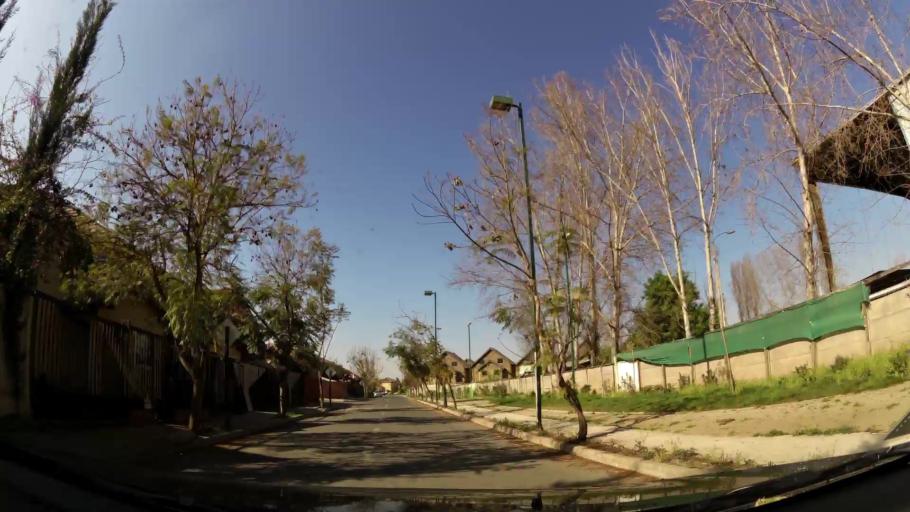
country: CL
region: Santiago Metropolitan
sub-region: Provincia de Chacabuco
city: Chicureo Abajo
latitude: -33.3551
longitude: -70.6794
